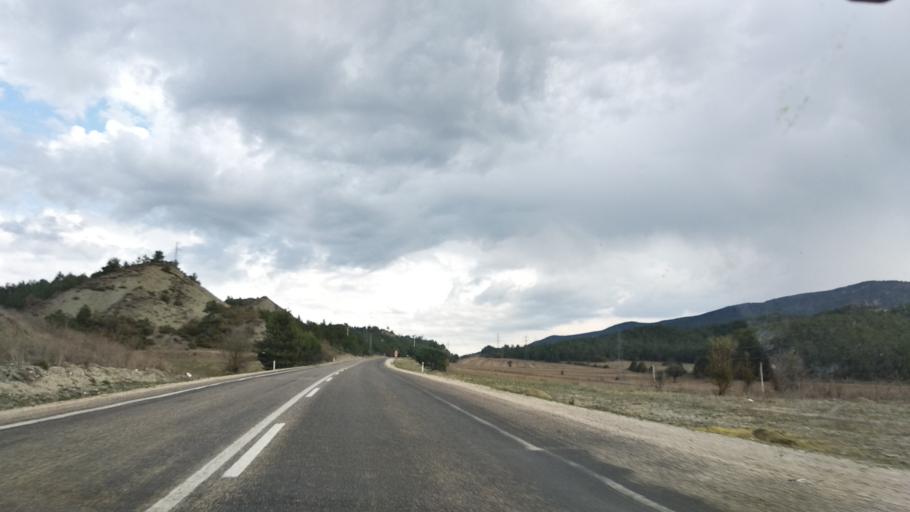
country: TR
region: Bolu
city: Mudurnu
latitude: 40.4837
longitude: 31.1802
